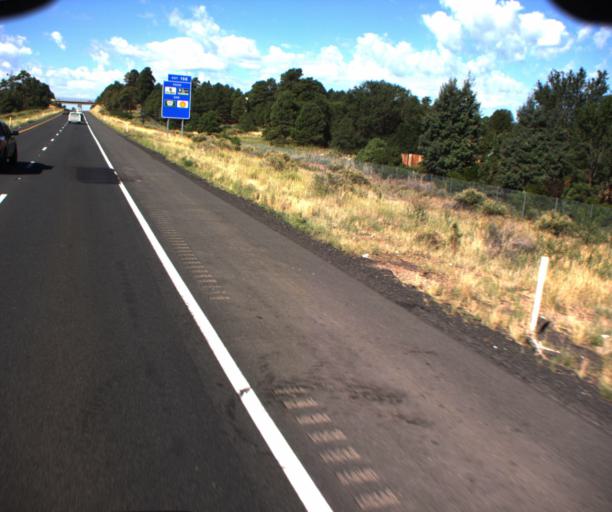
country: US
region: Arizona
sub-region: Coconino County
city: Flagstaff
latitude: 35.2055
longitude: -111.6040
